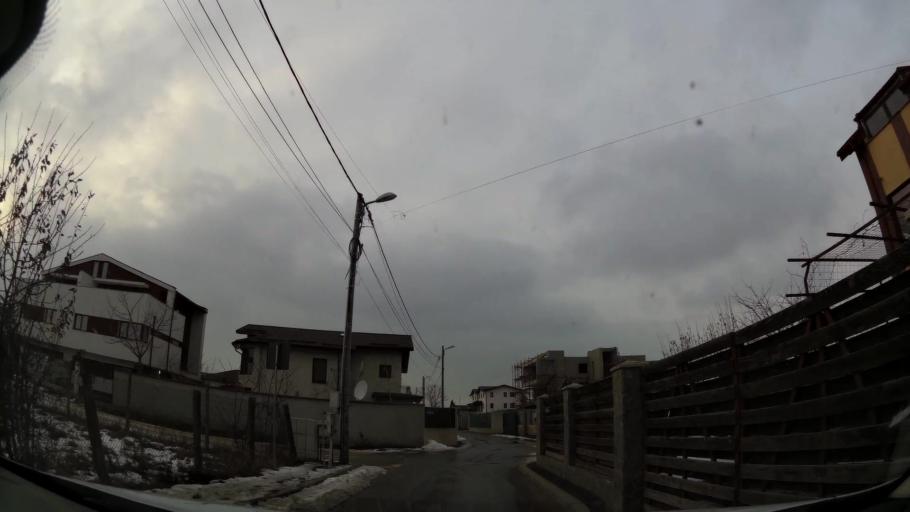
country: RO
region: Ilfov
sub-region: Voluntari City
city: Voluntari
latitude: 44.4970
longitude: 26.1655
